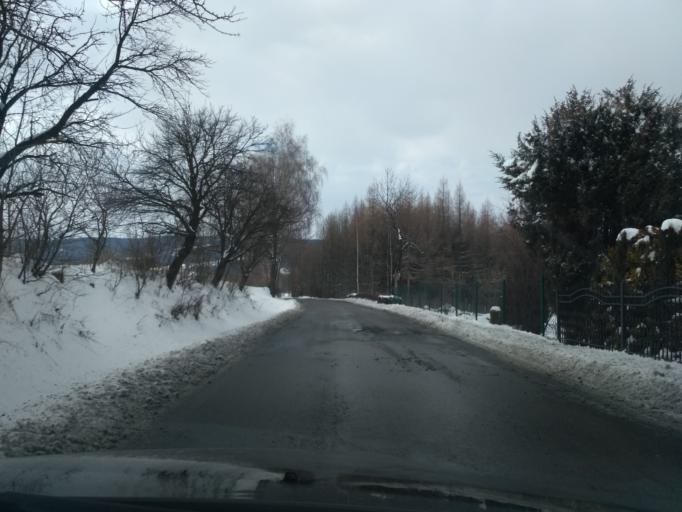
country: PL
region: Subcarpathian Voivodeship
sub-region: Powiat strzyzowski
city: Polomia
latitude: 49.8930
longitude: 21.8505
